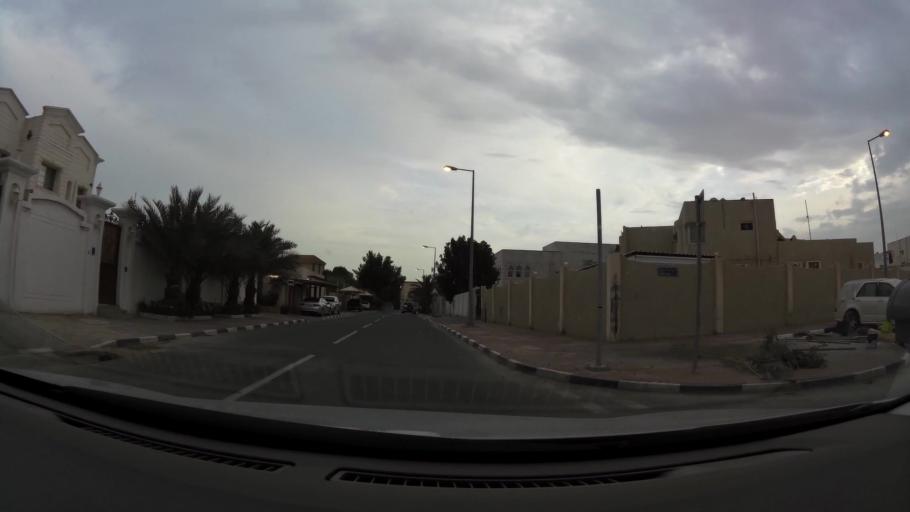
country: QA
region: Baladiyat ad Dawhah
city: Doha
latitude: 25.3400
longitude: 51.5100
